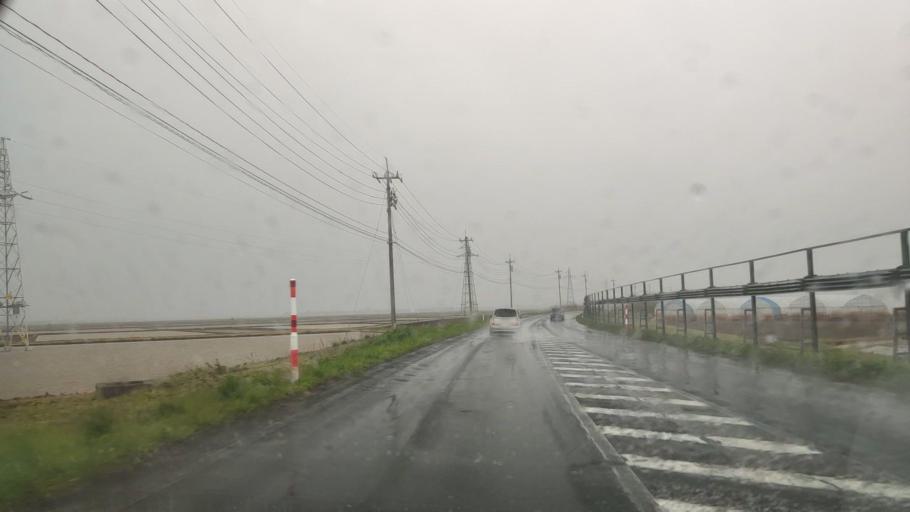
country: JP
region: Akita
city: Tenno
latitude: 39.9412
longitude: 139.9457
